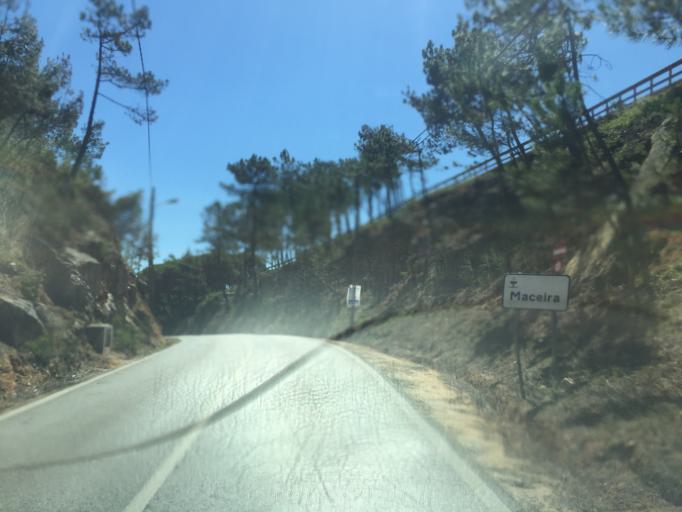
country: PT
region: Lisbon
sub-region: Torres Vedras
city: A dos Cunhados
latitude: 39.1794
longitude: -9.3450
